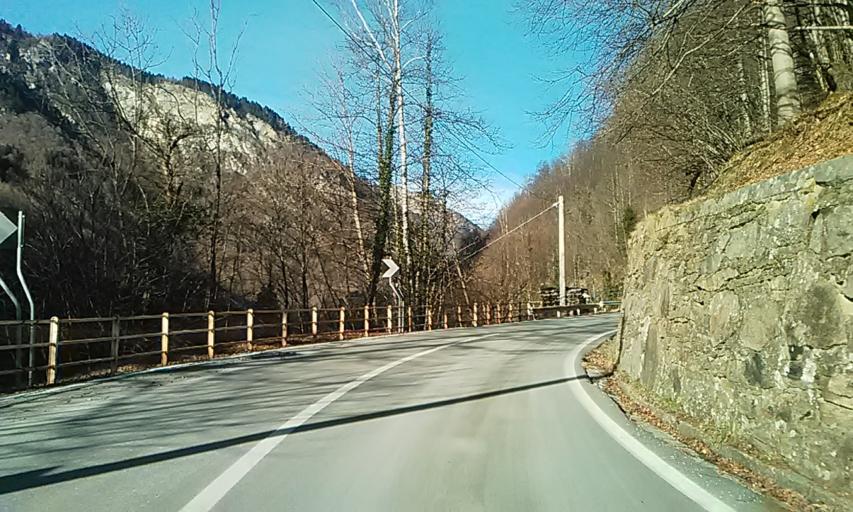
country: IT
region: Piedmont
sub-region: Provincia di Vercelli
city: Boccioleto
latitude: 45.8298
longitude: 8.0955
